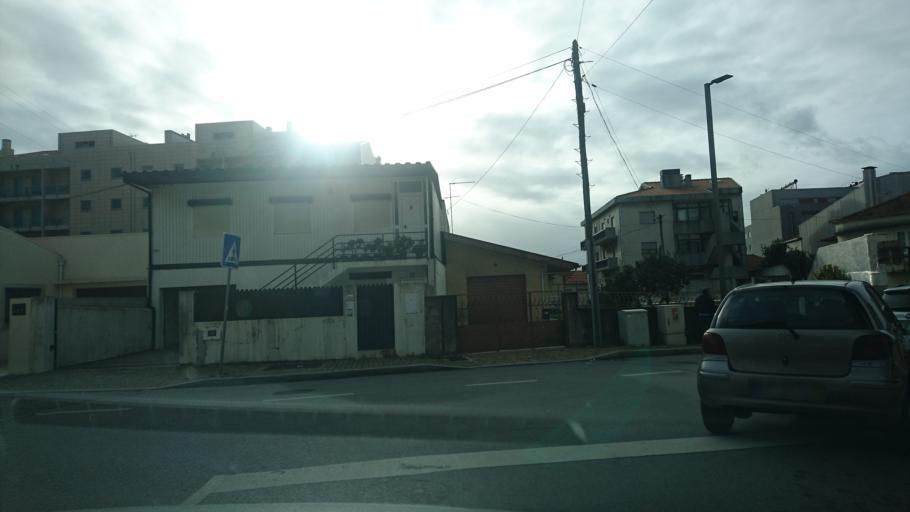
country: PT
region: Aveiro
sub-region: Ovar
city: Esmoriz
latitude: 40.9575
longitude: -8.6257
